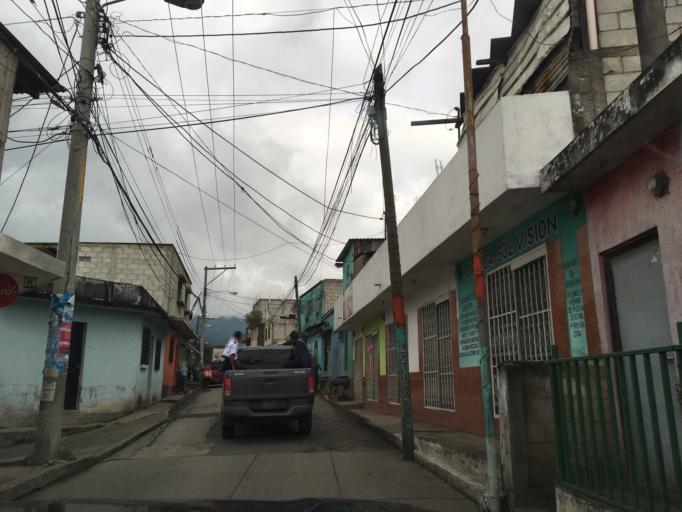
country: GT
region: Guatemala
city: Mixco
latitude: 14.6222
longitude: -90.5841
